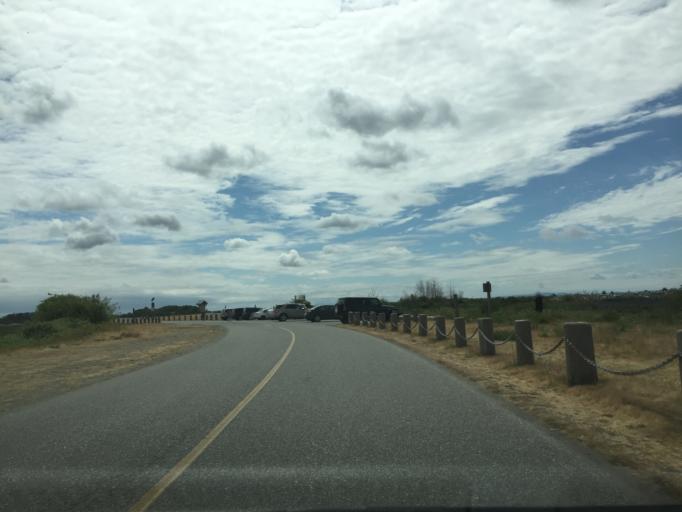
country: CA
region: British Columbia
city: Richmond
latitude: 49.2180
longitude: -123.2134
